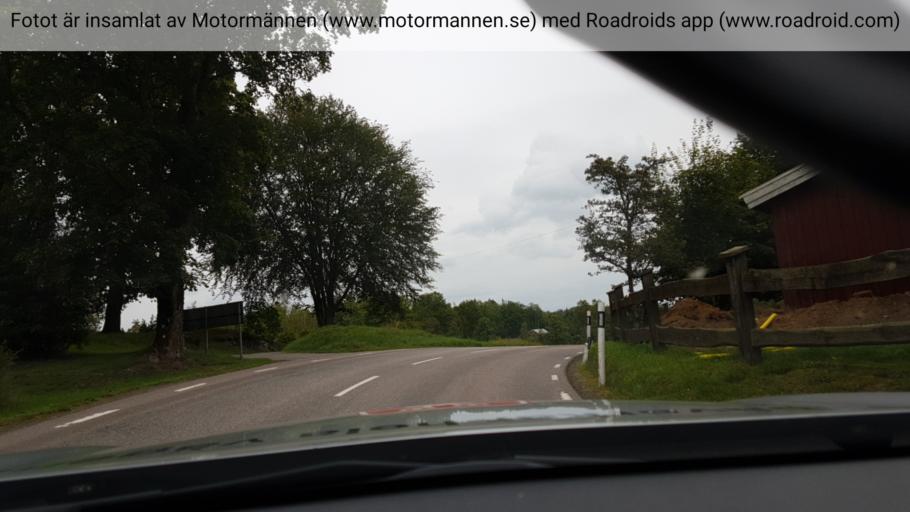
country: SE
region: Vaestra Goetaland
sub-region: Harryda Kommun
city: Hindas
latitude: 57.6085
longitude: 12.3417
